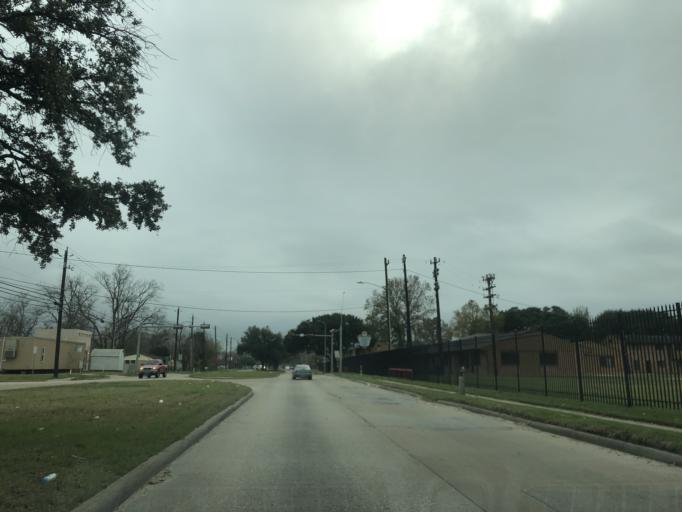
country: US
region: Texas
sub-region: Harris County
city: Jacinto City
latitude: 29.8292
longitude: -95.2845
